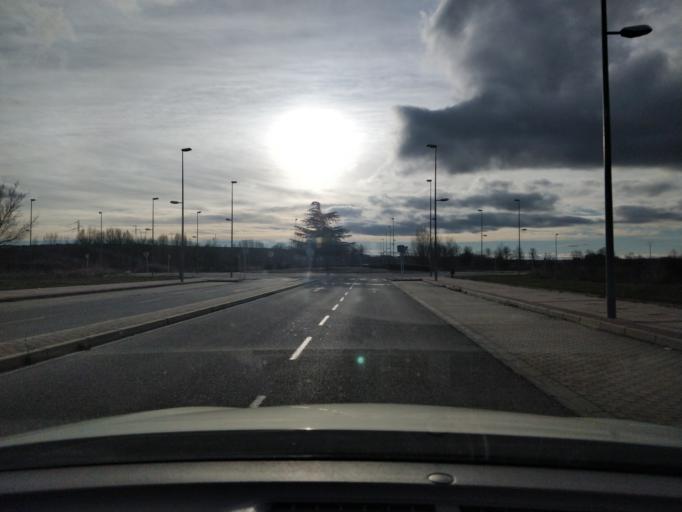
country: ES
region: Castille and Leon
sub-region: Provincia de Burgos
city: Villalbilla de Burgos
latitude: 42.3529
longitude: -3.7634
